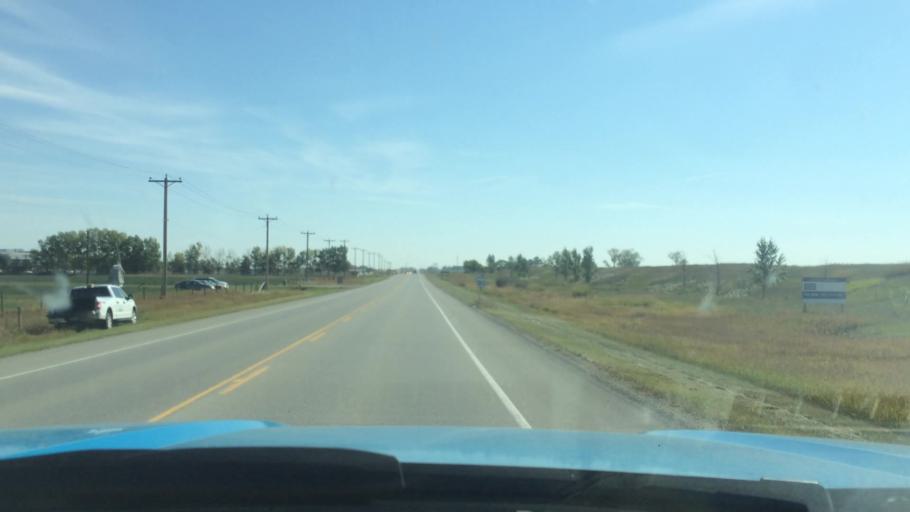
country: CA
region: Alberta
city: Airdrie
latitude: 51.2126
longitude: -113.9529
